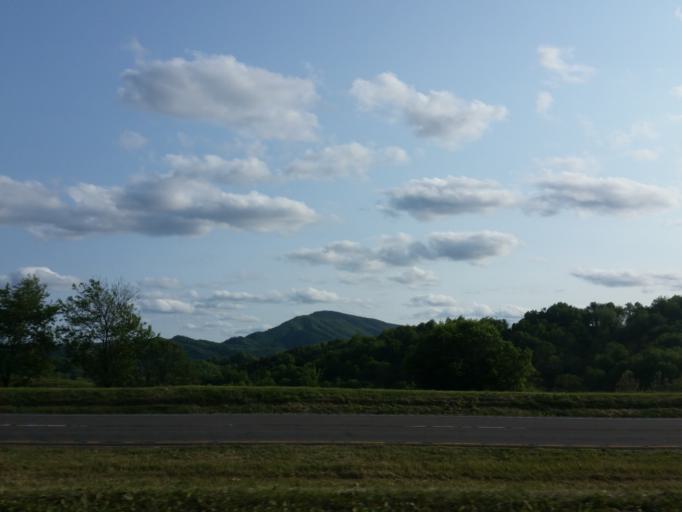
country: US
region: Virginia
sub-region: Tazewell County
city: Tazewell
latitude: 37.1202
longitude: -81.5582
